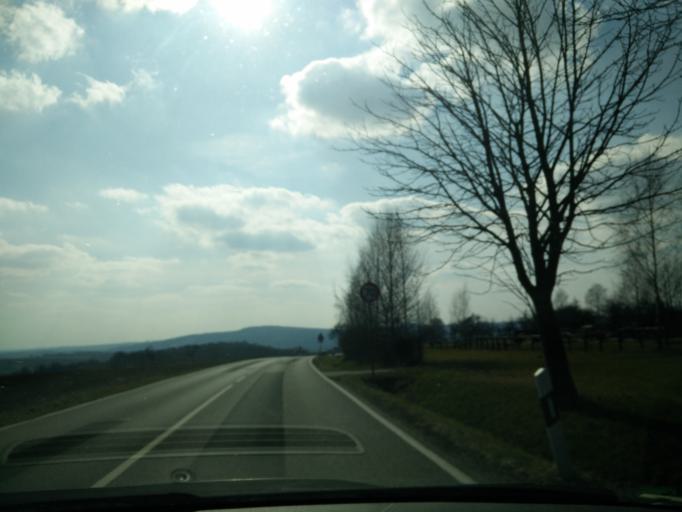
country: DE
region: Saxony
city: Zettlitz
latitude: 51.0597
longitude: 12.8397
